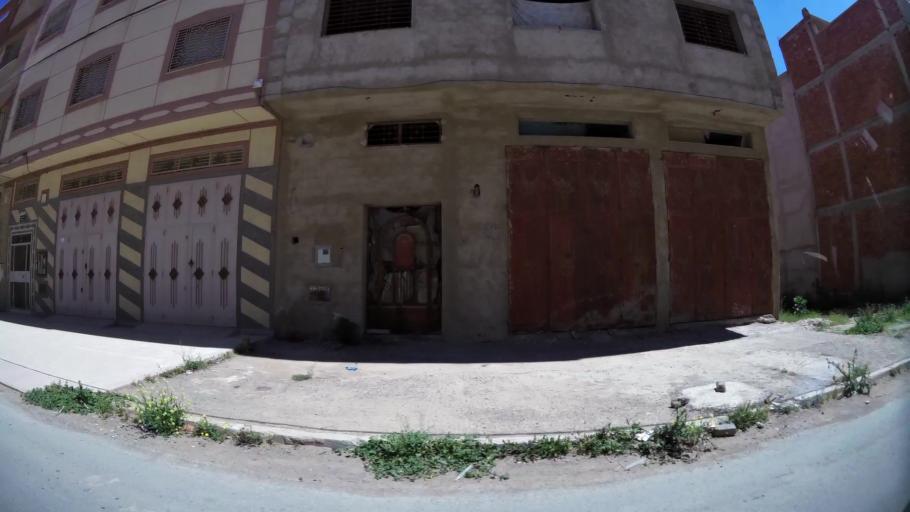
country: MA
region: Oriental
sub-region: Oujda-Angad
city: Oujda
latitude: 34.6603
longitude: -1.9473
